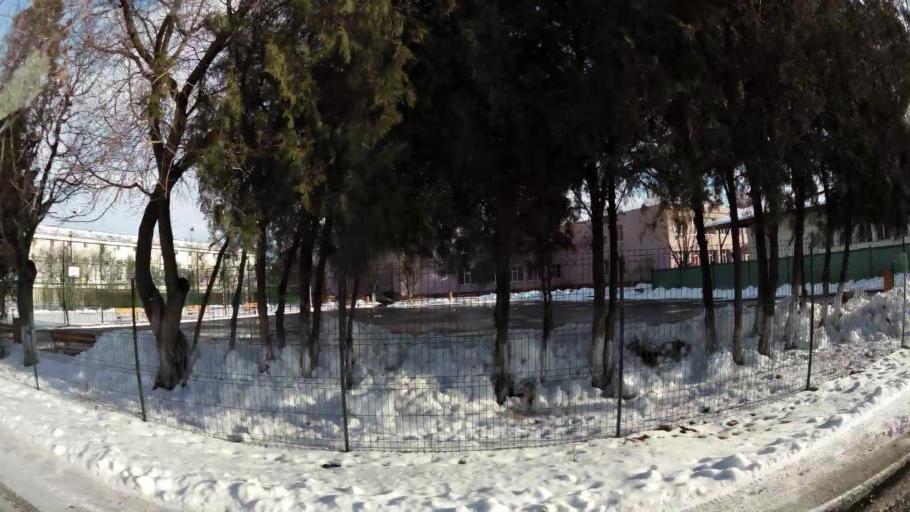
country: RO
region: Ilfov
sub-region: Voluntari City
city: Voluntari
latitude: 44.4923
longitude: 26.2013
